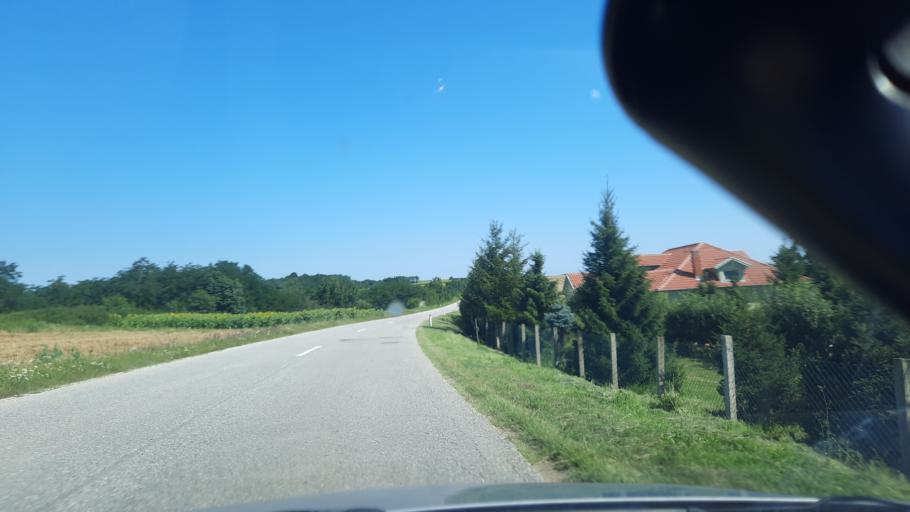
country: RS
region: Central Serbia
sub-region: Branicevski Okrug
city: Malo Crnice
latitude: 44.5819
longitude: 21.4158
